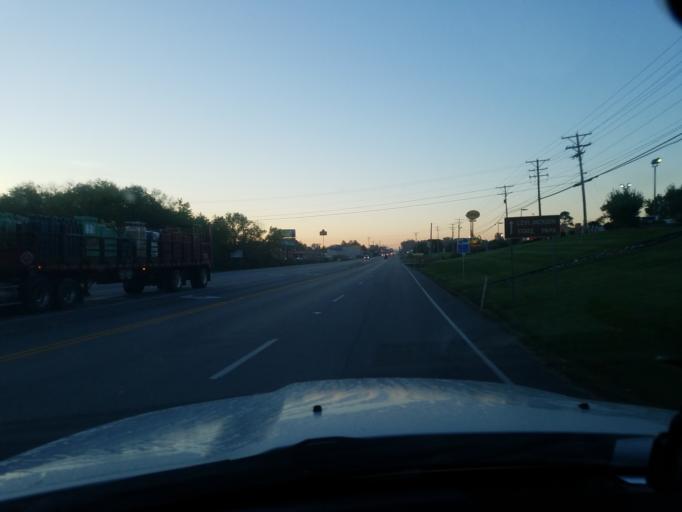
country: US
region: Kentucky
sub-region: Laurel County
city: London
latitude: 37.1071
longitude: -84.0723
